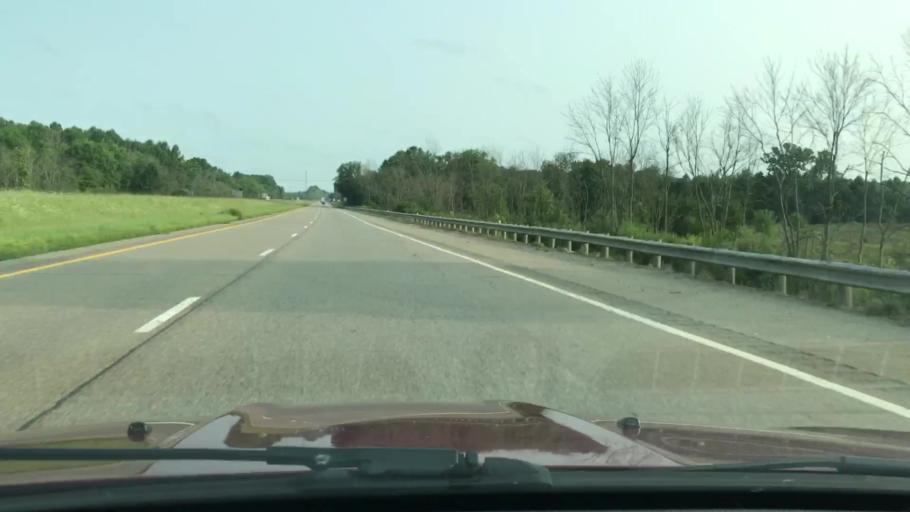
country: US
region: Ohio
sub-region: Guernsey County
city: Byesville
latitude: 39.9223
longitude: -81.5277
